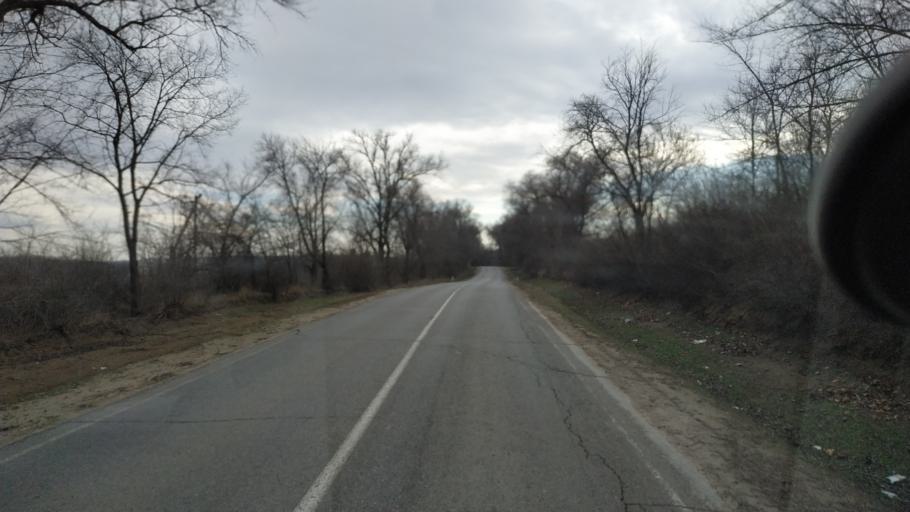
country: MD
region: Chisinau
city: Vadul lui Voda
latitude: 47.1247
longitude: 29.0638
